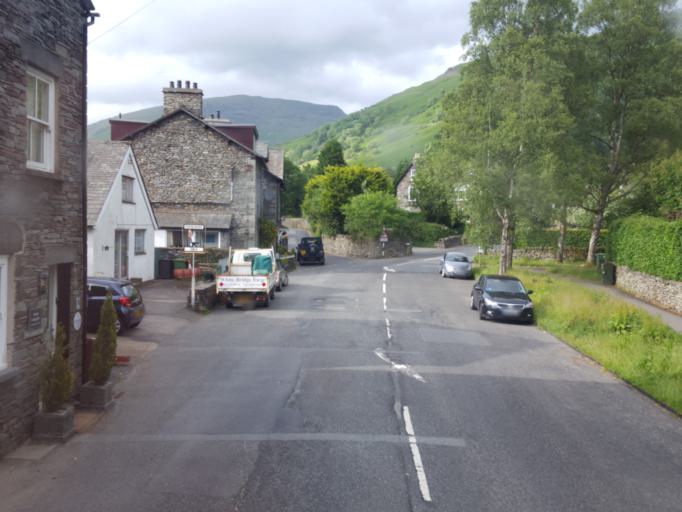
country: GB
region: England
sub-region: Cumbria
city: Ambleside
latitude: 54.4638
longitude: -3.0224
